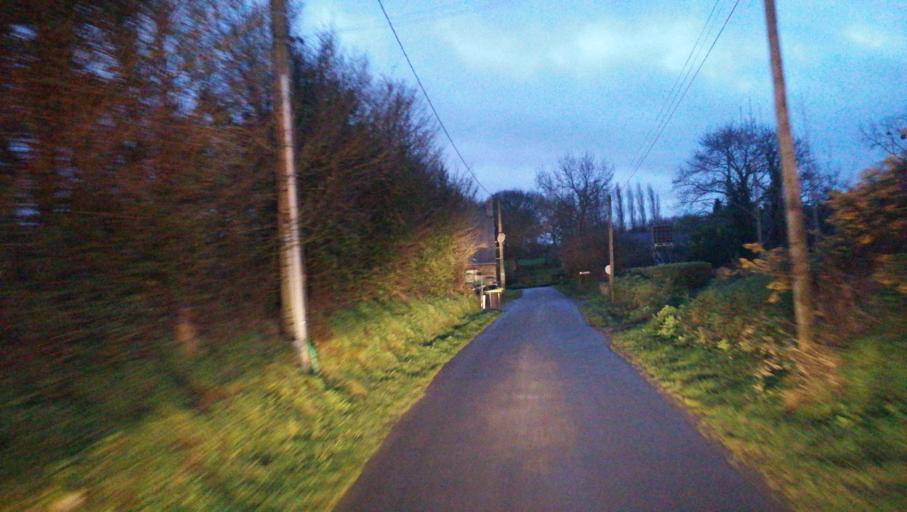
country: FR
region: Brittany
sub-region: Departement des Cotes-d'Armor
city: Plehedel
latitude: 48.6726
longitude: -3.0351
